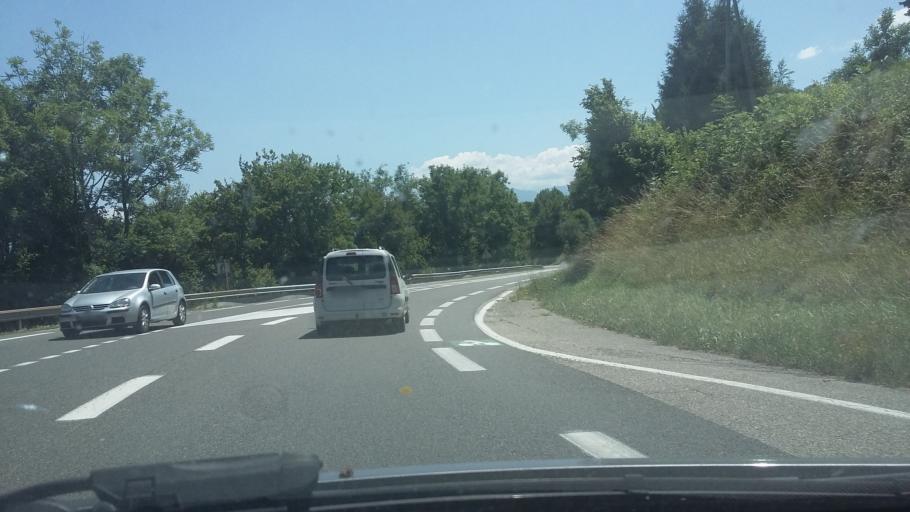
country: FR
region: Rhone-Alpes
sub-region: Departement de la Savoie
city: Le Bourget-du-Lac
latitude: 45.6756
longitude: 5.8531
